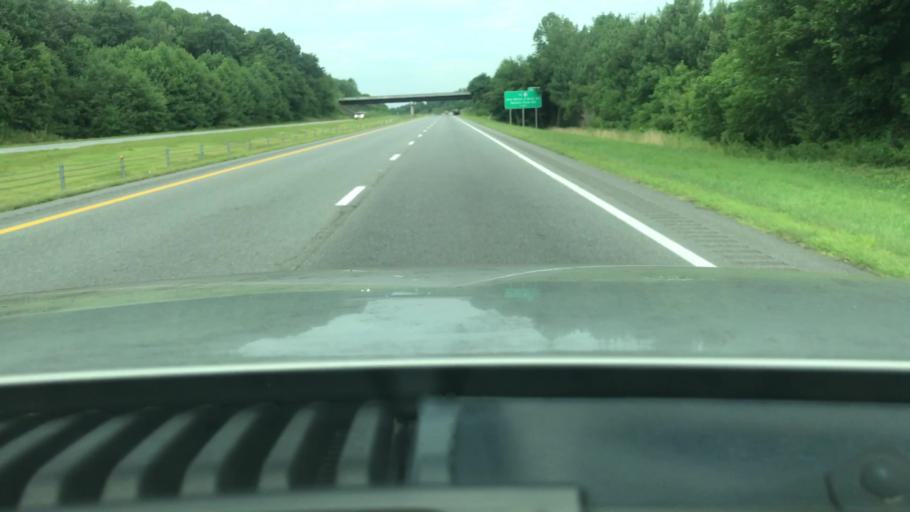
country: US
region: North Carolina
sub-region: Surry County
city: Elkin
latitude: 36.1608
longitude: -80.9718
